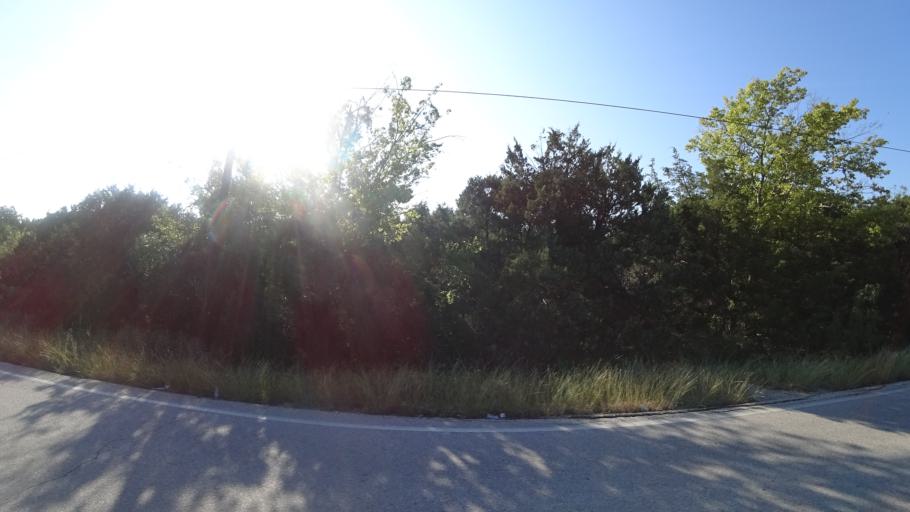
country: US
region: Texas
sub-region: Travis County
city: Austin
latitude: 30.3201
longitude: -97.6589
